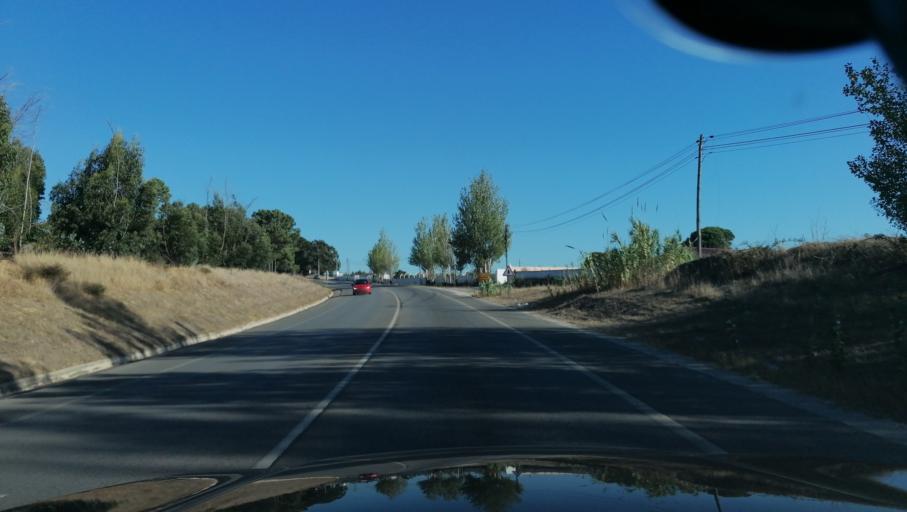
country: PT
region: Setubal
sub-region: Moita
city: Moita
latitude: 38.6344
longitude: -8.9707
